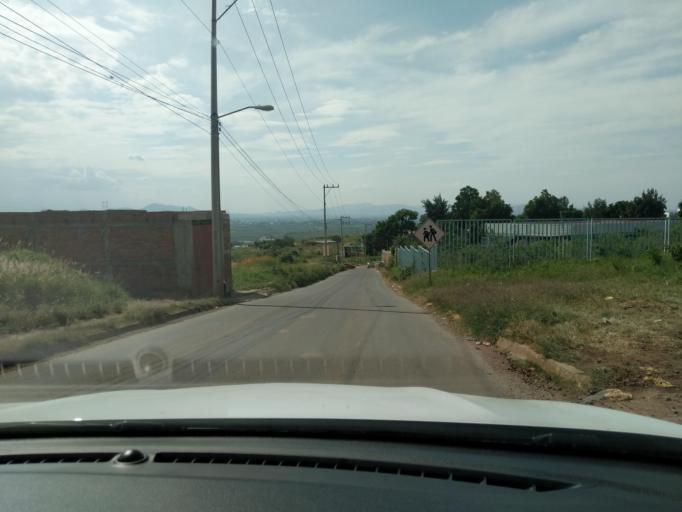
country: MX
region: Jalisco
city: San Jose del Castillo
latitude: 20.5254
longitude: -103.2319
